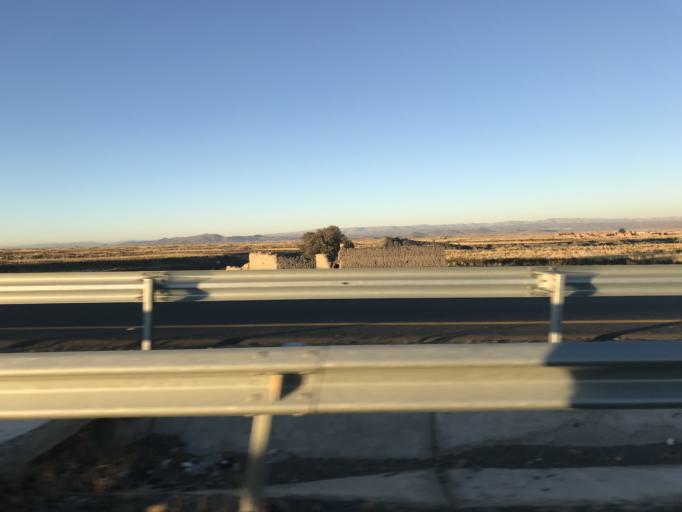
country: BO
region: La Paz
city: Batallas
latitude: -16.3114
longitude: -68.4543
